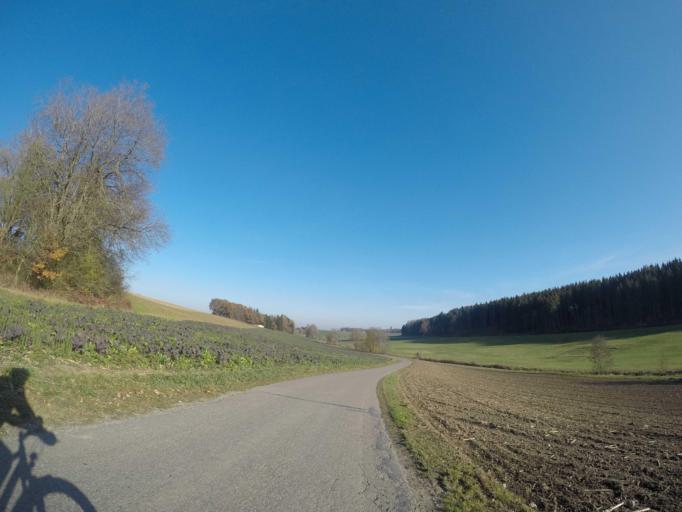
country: DE
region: Baden-Wuerttemberg
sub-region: Tuebingen Region
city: Unterwachingen
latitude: 48.1881
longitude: 9.6445
